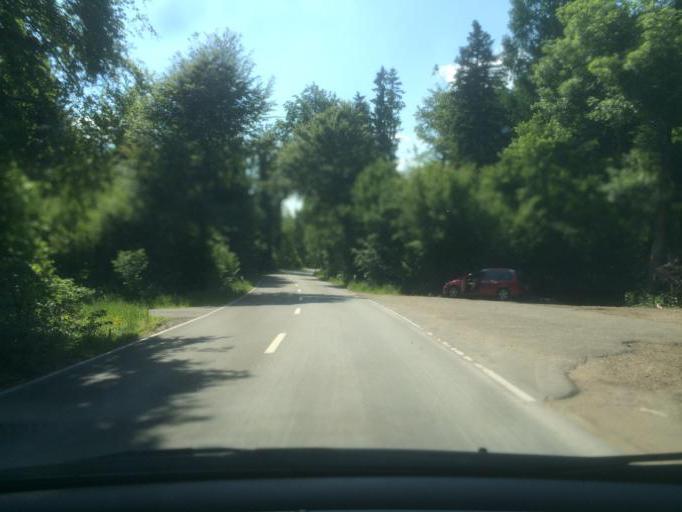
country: CH
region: Zurich
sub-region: Bezirk Uster
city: Uster / Ober-Uster
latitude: 47.3457
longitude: 8.7543
